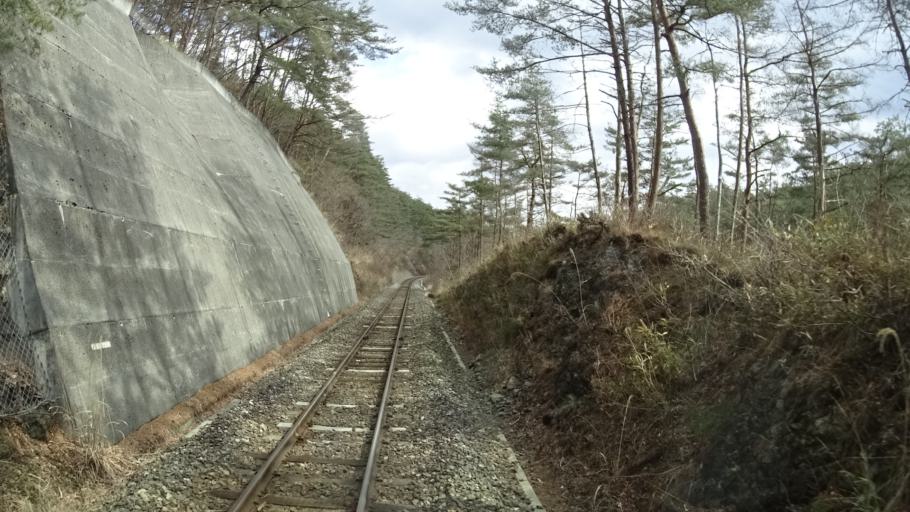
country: JP
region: Iwate
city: Tono
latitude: 39.3361
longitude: 141.3557
